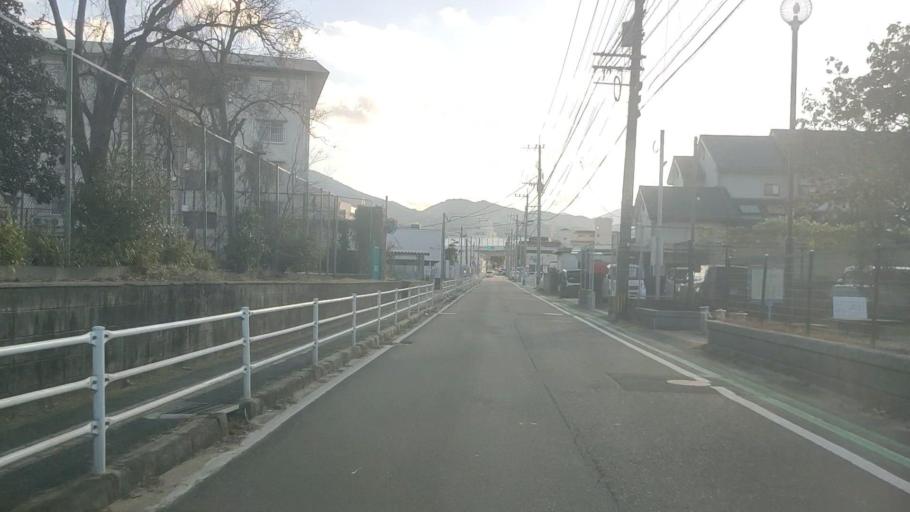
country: JP
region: Fukuoka
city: Fukuoka-shi
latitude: 33.5483
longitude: 130.3573
